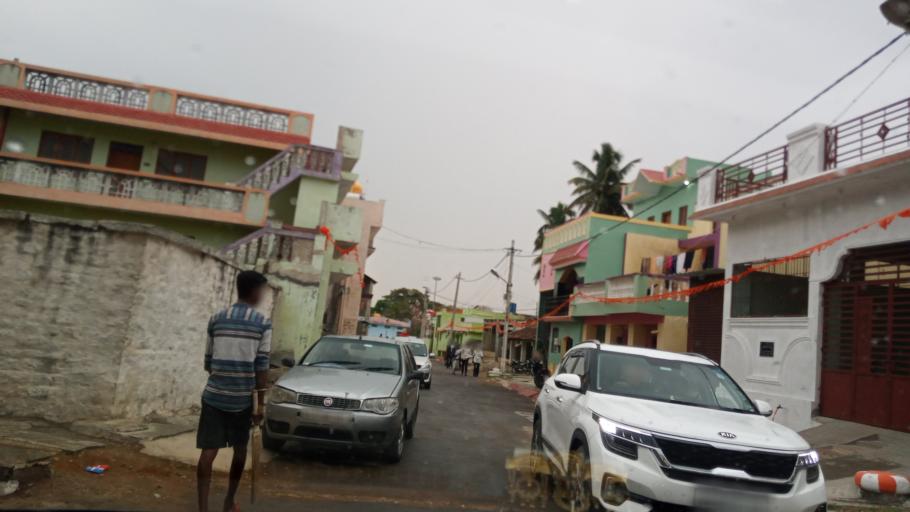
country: IN
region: Karnataka
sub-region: Kolar
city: Mulbagal
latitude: 13.1074
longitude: 78.3278
